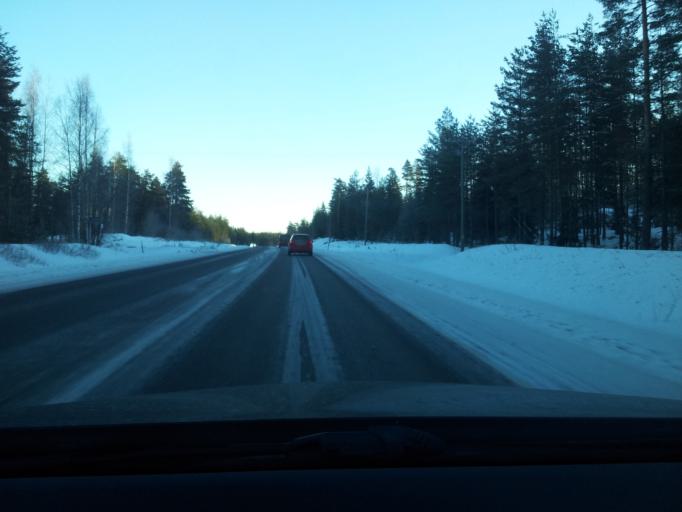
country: FI
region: Uusimaa
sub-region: Helsinki
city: Vihti
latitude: 60.3619
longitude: 24.3534
